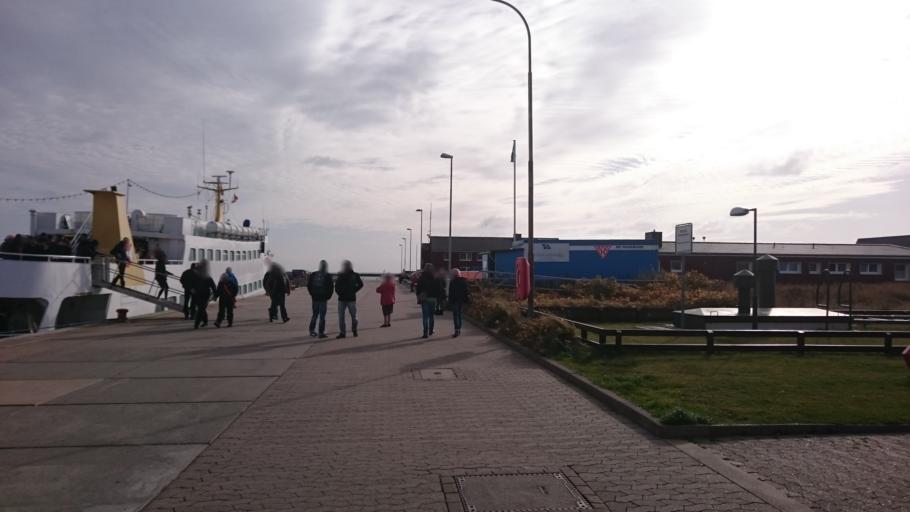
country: DE
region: Schleswig-Holstein
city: Helgoland
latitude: 54.1759
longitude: 7.8926
